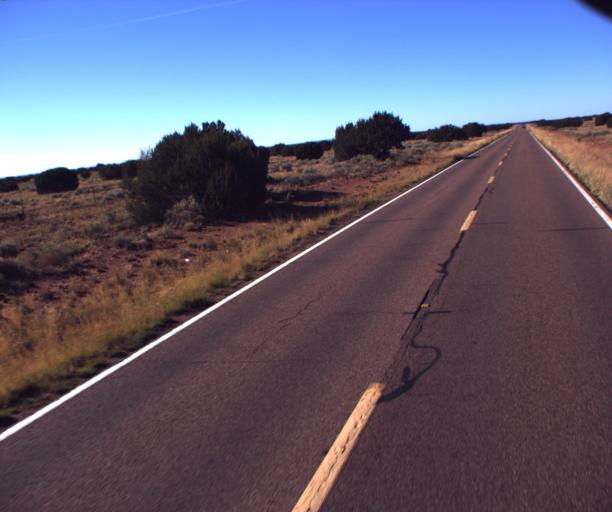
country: US
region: Arizona
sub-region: Navajo County
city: Heber-Overgaard
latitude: 34.5822
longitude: -110.4039
